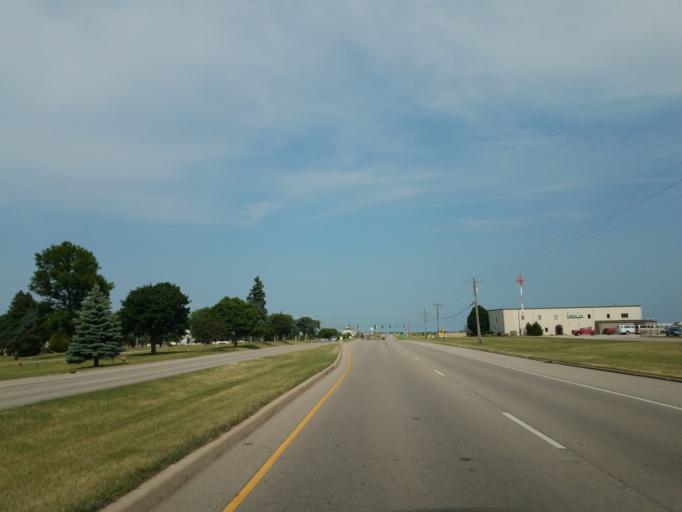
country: US
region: Illinois
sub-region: McLean County
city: Bloomington
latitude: 40.4883
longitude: -88.9267
